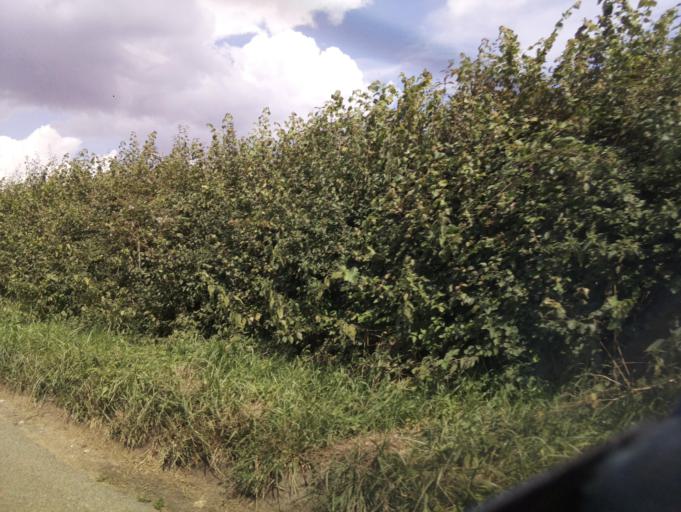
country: GB
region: England
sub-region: Oxfordshire
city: Shrivenham
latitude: 51.5829
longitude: -1.6543
